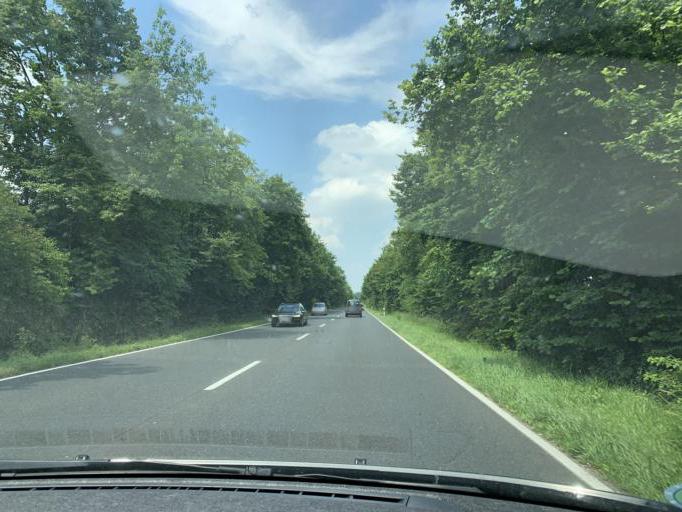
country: DE
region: North Rhine-Westphalia
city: Niedermerz
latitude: 50.8546
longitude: 6.2333
